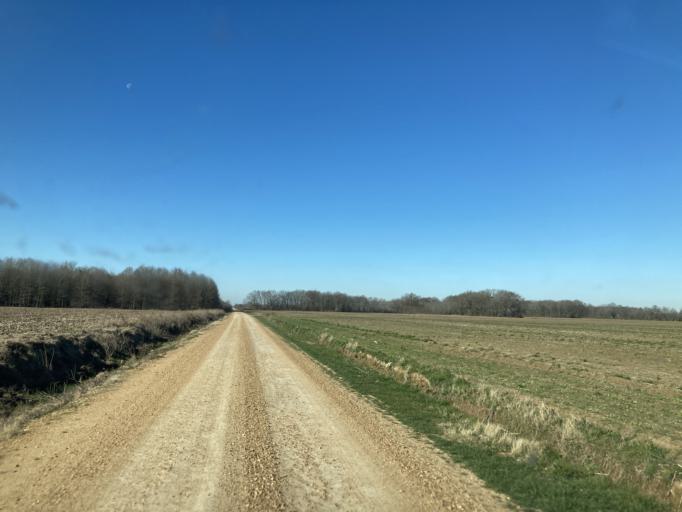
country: US
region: Mississippi
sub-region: Yazoo County
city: Yazoo City
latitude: 32.9519
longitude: -90.6087
